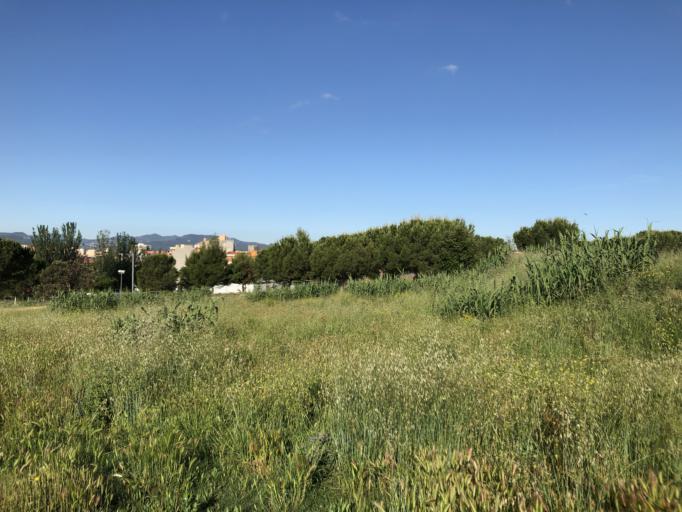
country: ES
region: Catalonia
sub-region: Provincia de Barcelona
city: Rubi
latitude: 41.4918
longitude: 2.0414
